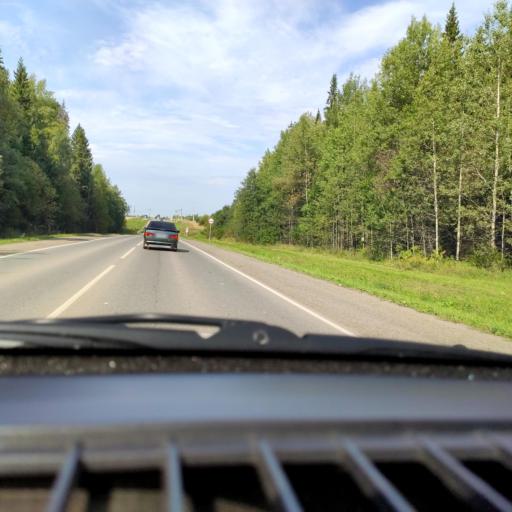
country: RU
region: Perm
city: Ust'-Kachka
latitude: 57.9239
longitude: 55.7631
